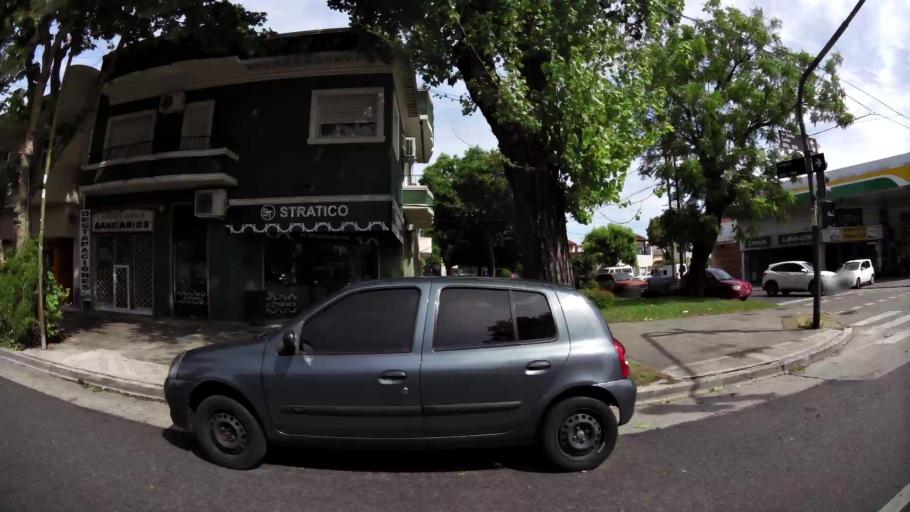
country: AR
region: Buenos Aires
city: San Justo
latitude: -34.6528
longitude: -58.5169
